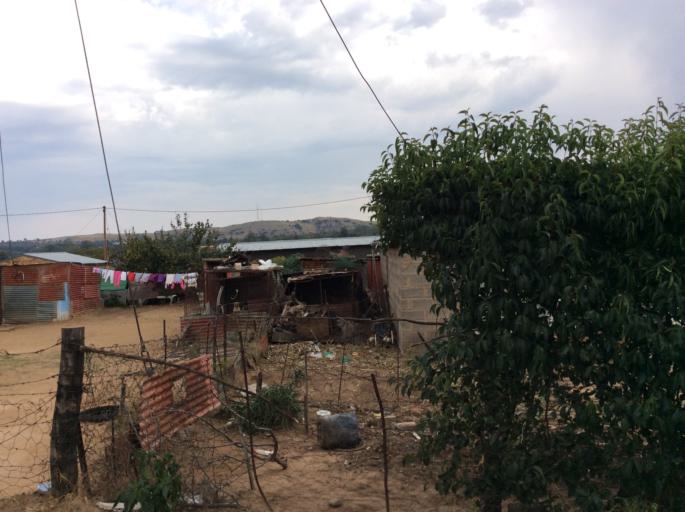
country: ZA
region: Orange Free State
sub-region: Xhariep District Municipality
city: Dewetsdorp
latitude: -29.5796
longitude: 26.6808
